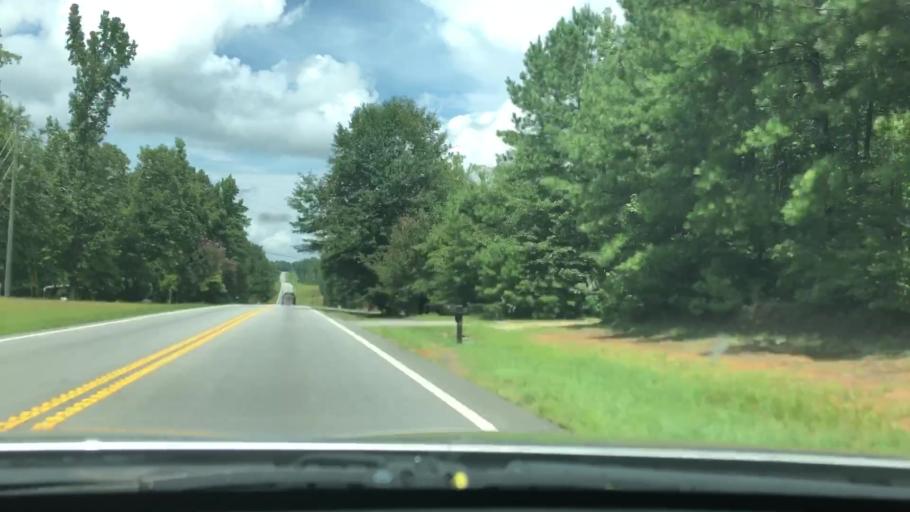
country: US
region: Georgia
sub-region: Lamar County
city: Barnesville
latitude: 33.1190
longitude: -84.1542
